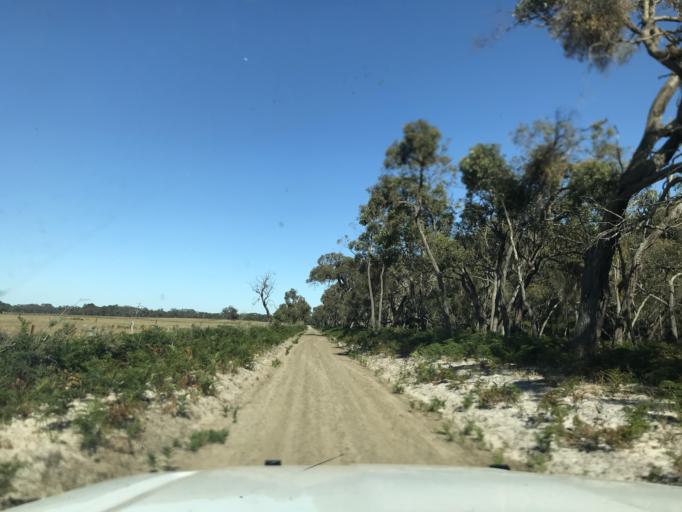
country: AU
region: South Australia
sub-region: Wattle Range
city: Penola
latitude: -37.0816
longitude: 141.3951
